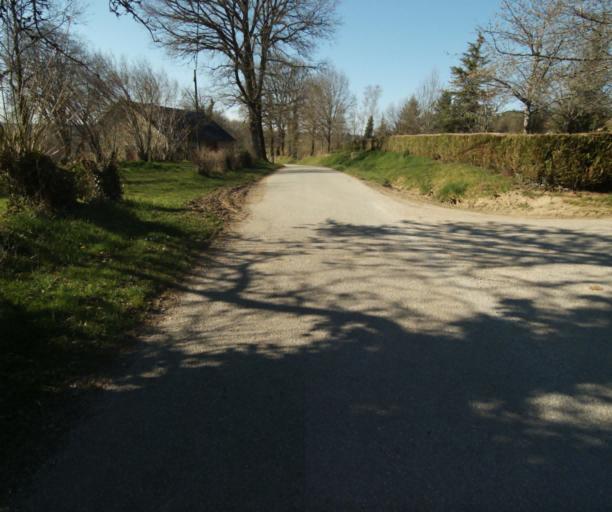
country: FR
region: Limousin
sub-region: Departement de la Correze
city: Chamboulive
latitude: 45.4801
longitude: 1.6890
